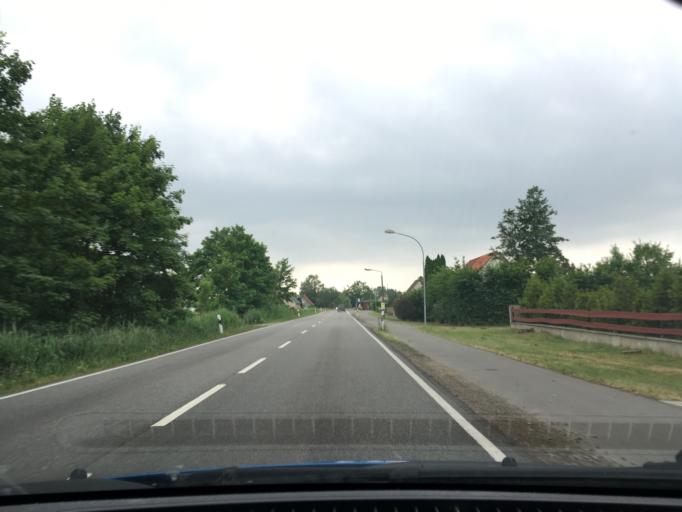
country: DE
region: Lower Saxony
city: Lubbow
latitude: 52.8873
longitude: 11.1756
